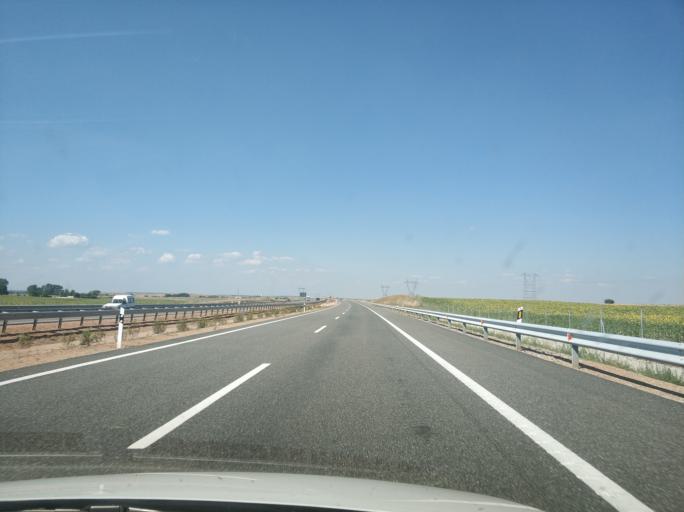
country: ES
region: Castille and Leon
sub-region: Provincia de Zamora
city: San Cebrian de Castro
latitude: 41.7312
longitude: -5.7722
